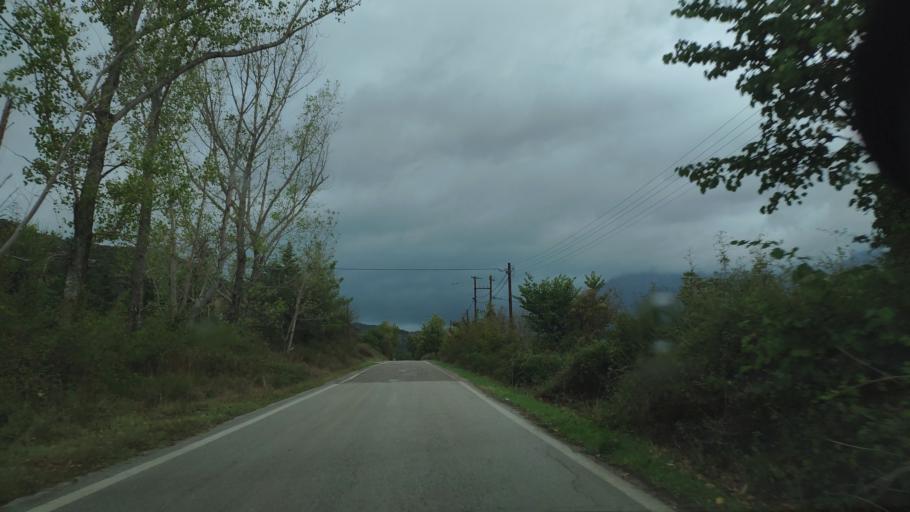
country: GR
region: West Greece
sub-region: Nomos Aitolias kai Akarnanias
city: Krikellos
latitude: 38.9900
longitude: 21.3157
